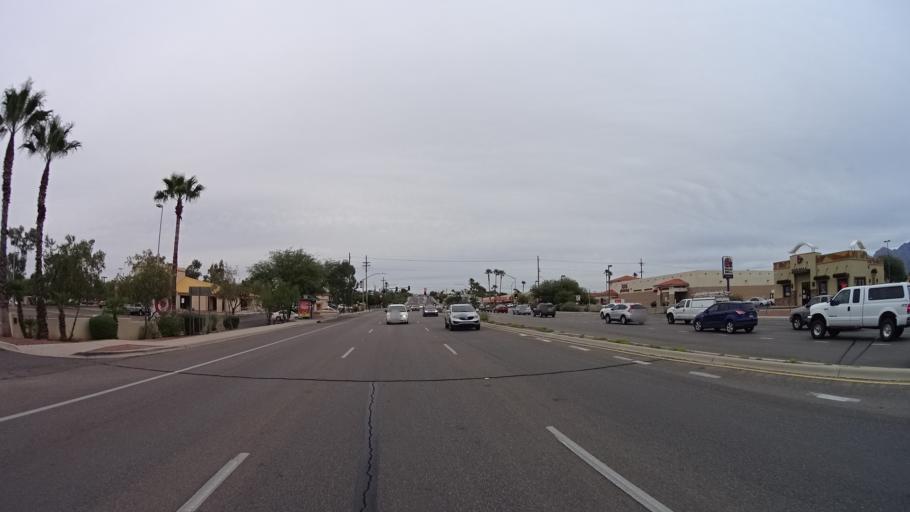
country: US
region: Arizona
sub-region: Pima County
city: Casas Adobes
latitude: 32.3364
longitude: -111.0470
